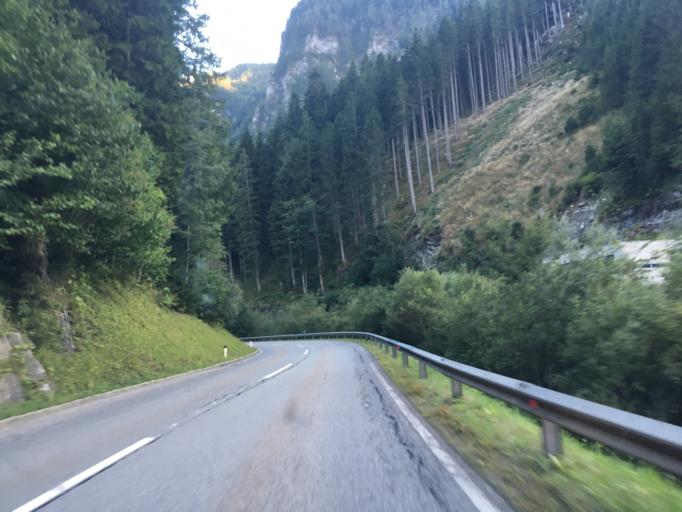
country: AT
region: Styria
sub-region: Politischer Bezirk Liezen
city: Trieben
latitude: 47.4628
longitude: 14.4861
